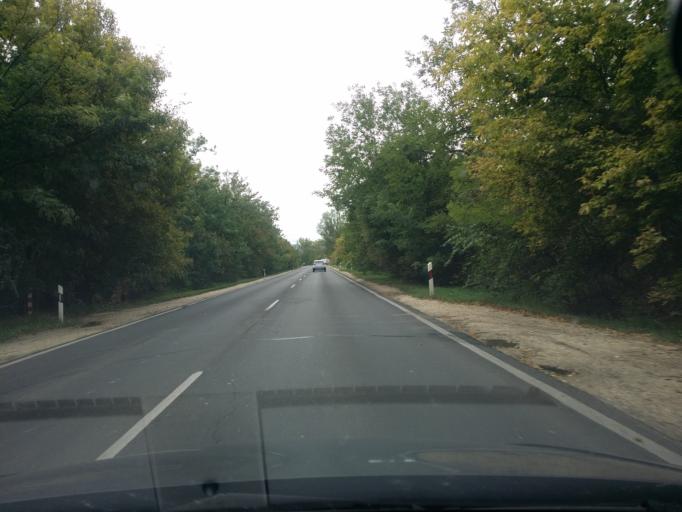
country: HU
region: Pest
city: Dunakeszi
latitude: 47.6224
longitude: 19.1175
